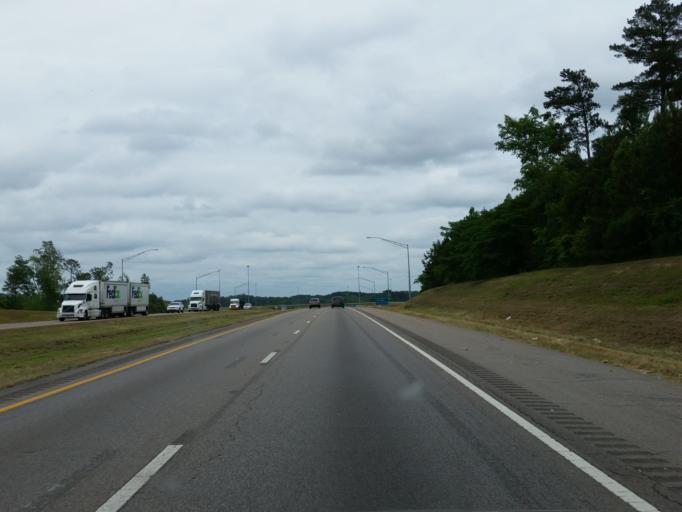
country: US
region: Mississippi
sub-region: Lauderdale County
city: Meridian
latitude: 32.3753
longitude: -88.6616
